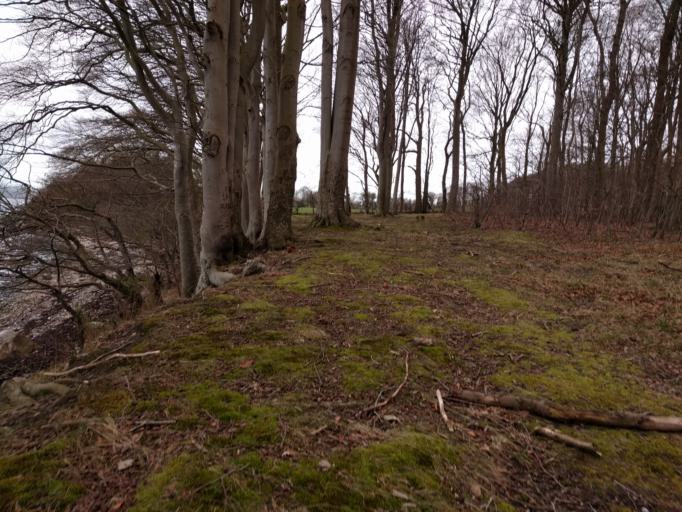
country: DK
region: South Denmark
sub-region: Aabenraa Kommune
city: Lojt Kirkeby
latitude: 55.1267
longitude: 9.5099
